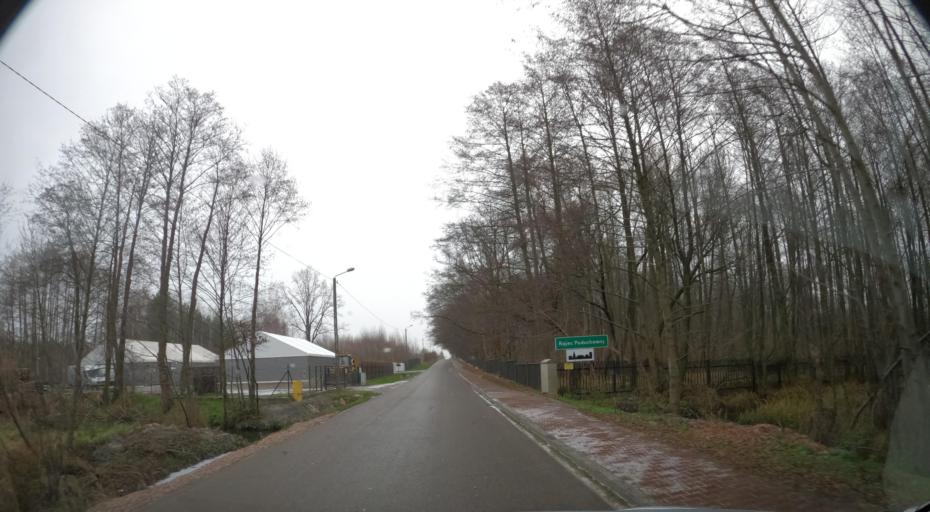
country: PL
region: Masovian Voivodeship
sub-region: Powiat radomski
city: Jastrzebia
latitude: 51.4272
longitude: 21.2337
